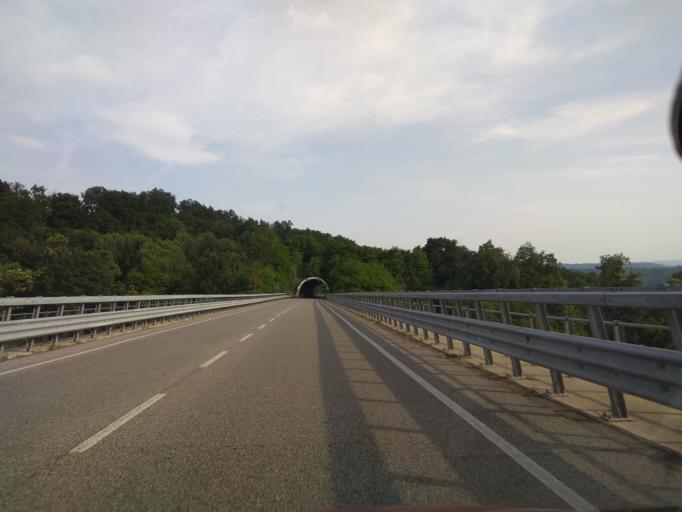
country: IT
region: Piedmont
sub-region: Provincia di Biella
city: Quaregna
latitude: 45.5941
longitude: 8.1702
